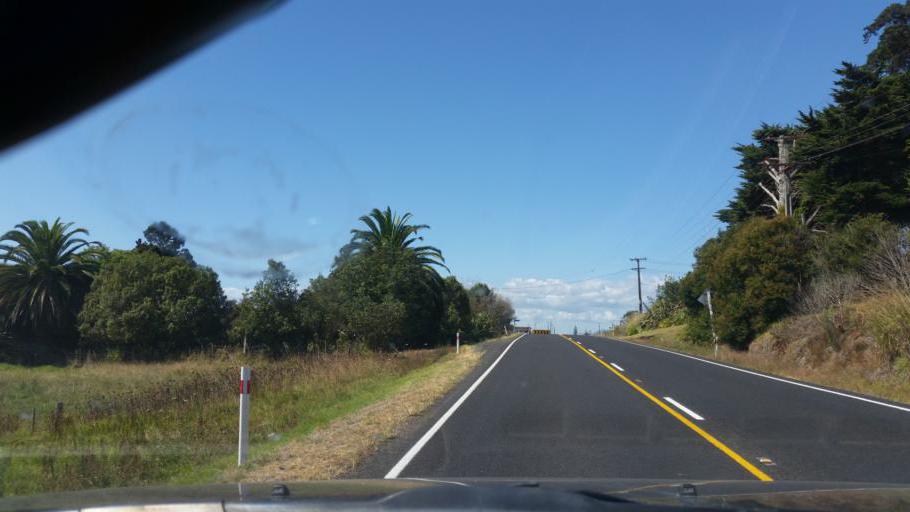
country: NZ
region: Northland
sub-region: Kaipara District
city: Dargaville
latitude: -35.9528
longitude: 173.8549
